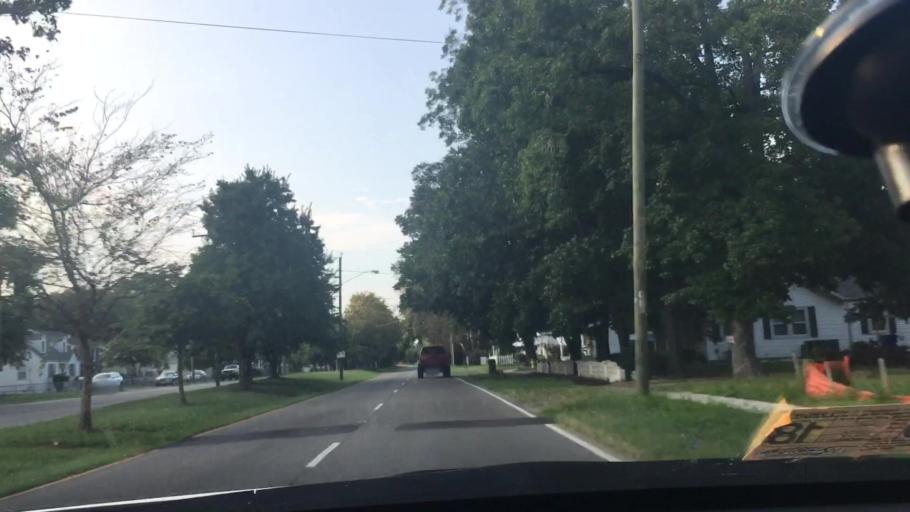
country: US
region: Virginia
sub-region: City of Norfolk
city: Norfolk
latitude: 36.9344
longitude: -76.2444
